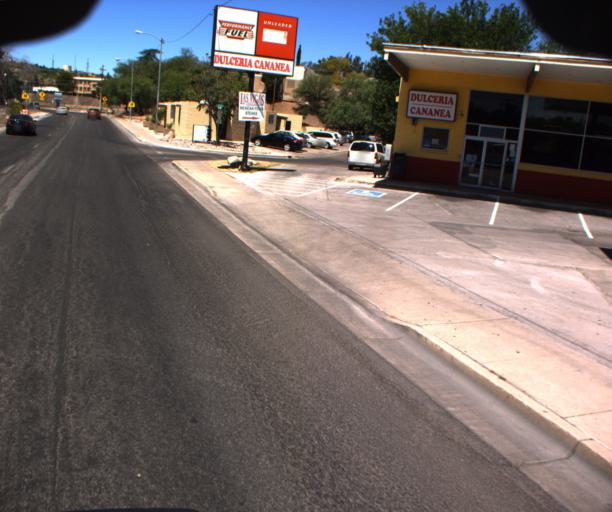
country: US
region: Arizona
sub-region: Santa Cruz County
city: Nogales
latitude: 31.3408
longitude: -110.9371
